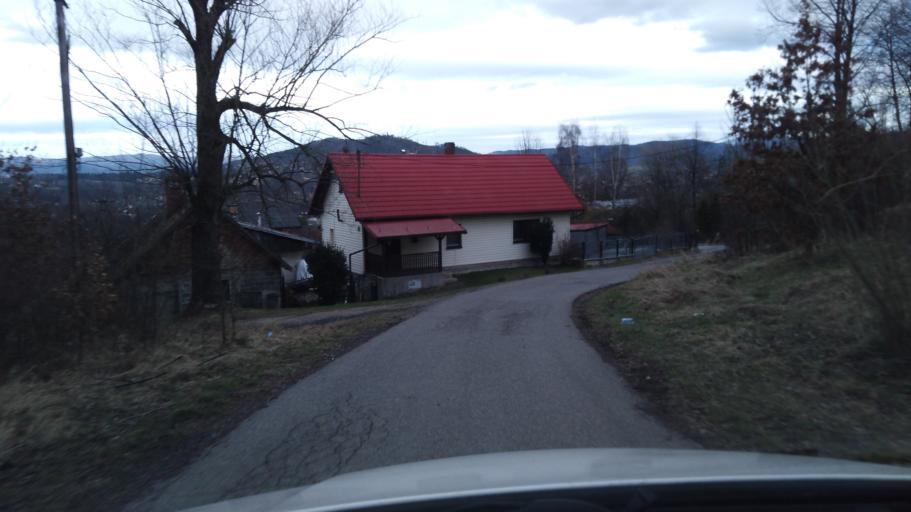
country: PL
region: Silesian Voivodeship
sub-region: Powiat zywiecki
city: Trzebinia
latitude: 49.6637
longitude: 19.2163
